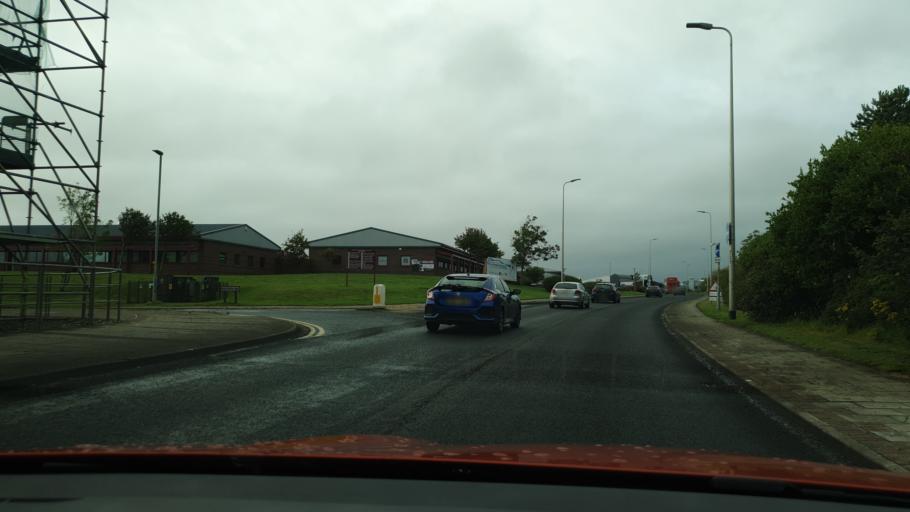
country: GB
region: England
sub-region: Cumbria
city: Barrow in Furness
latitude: 54.1168
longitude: -3.2415
